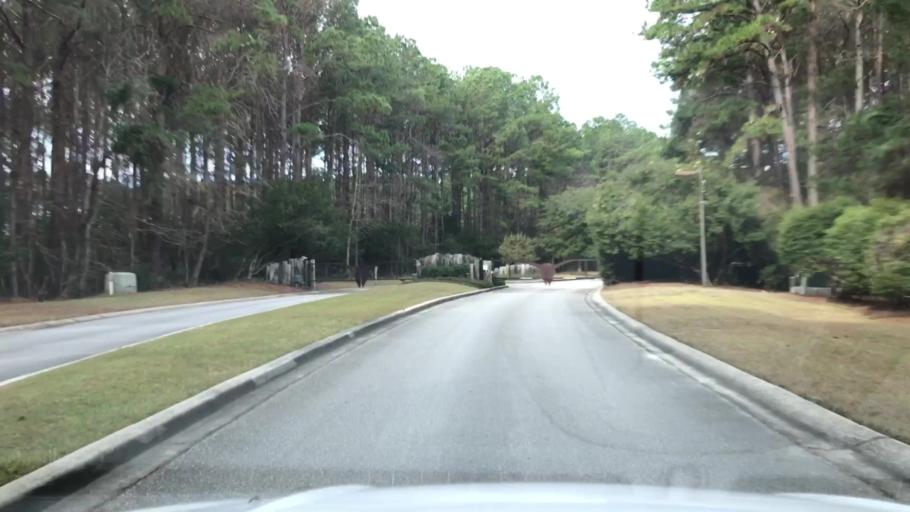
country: US
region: South Carolina
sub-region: Charleston County
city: Isle of Palms
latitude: 32.9066
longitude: -79.7207
